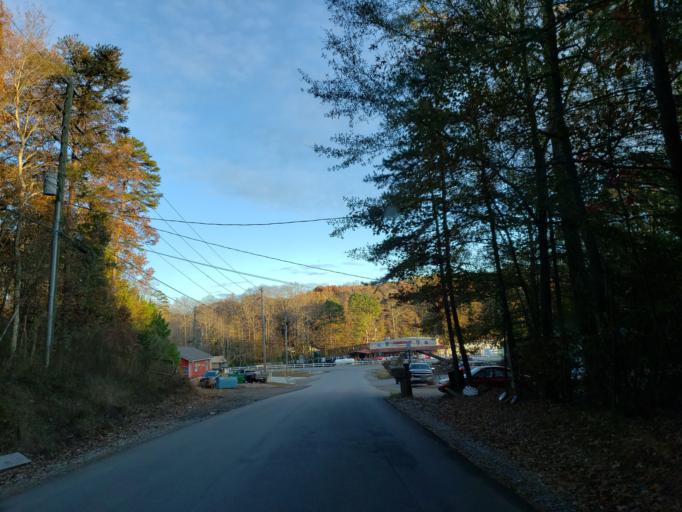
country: US
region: Georgia
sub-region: Cherokee County
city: Ball Ground
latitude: 34.2804
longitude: -84.2973
